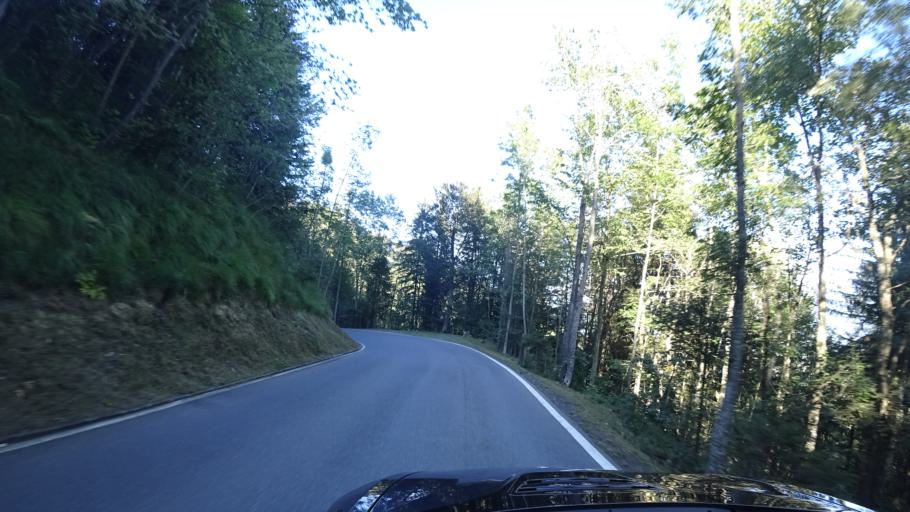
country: CH
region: Obwalden
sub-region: Obwalden
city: Giswil
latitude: 46.8315
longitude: 8.1343
